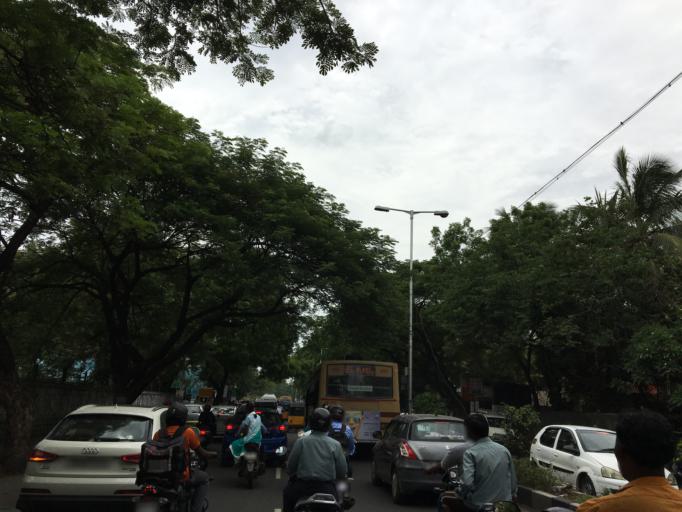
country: IN
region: Tamil Nadu
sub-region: Kancheepuram
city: Alandur
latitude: 12.9924
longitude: 80.2189
